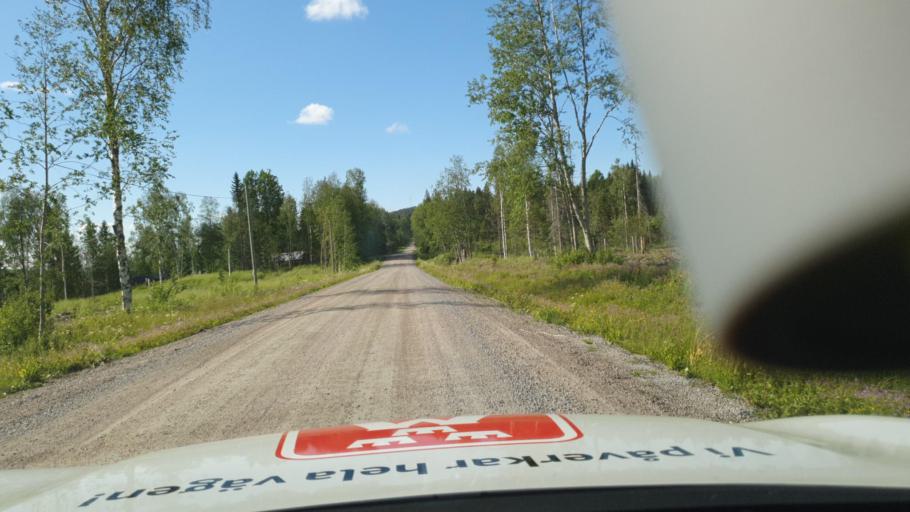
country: SE
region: Vaesterbotten
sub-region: Vannas Kommun
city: Vaennaes
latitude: 63.7801
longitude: 19.6352
